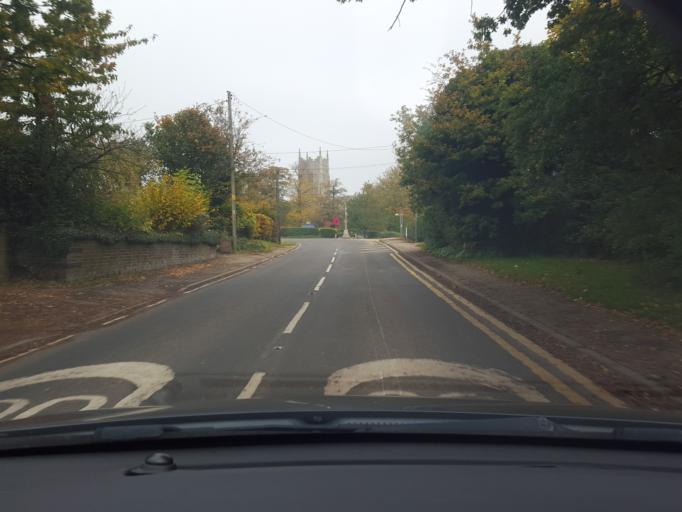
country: GB
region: England
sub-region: Essex
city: Alresford
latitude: 51.8945
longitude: 1.0270
